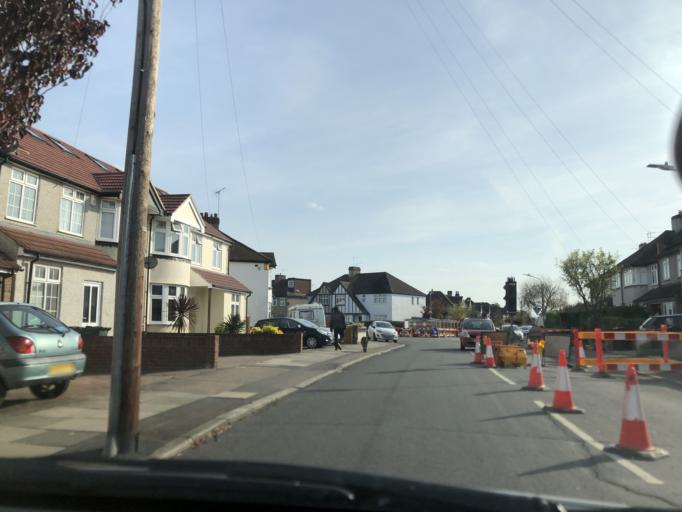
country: GB
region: England
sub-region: Kent
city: Dartford
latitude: 51.4433
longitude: 0.1866
